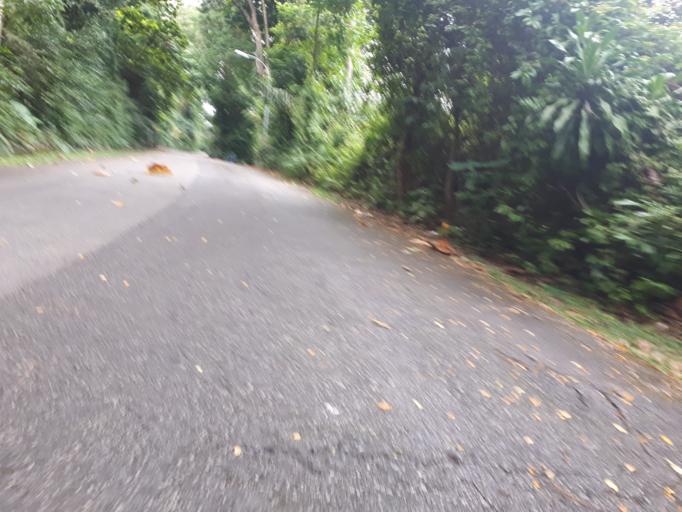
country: SG
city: Singapore
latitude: 1.3138
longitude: 103.8345
